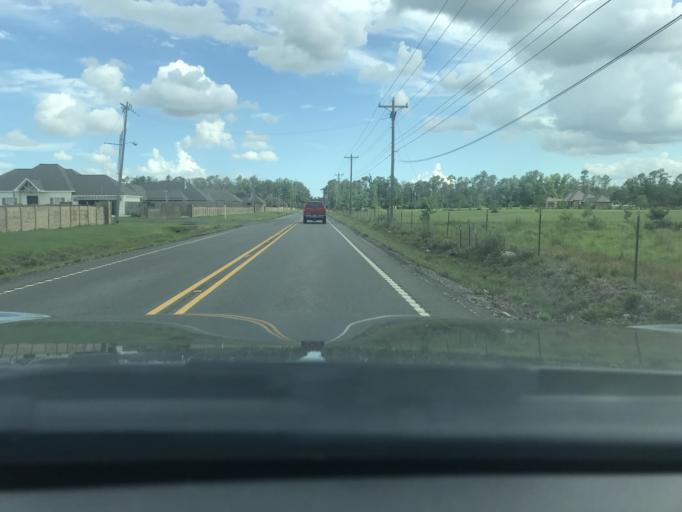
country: US
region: Louisiana
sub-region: Calcasieu Parish
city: Moss Bluff
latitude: 30.3118
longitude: -93.2584
